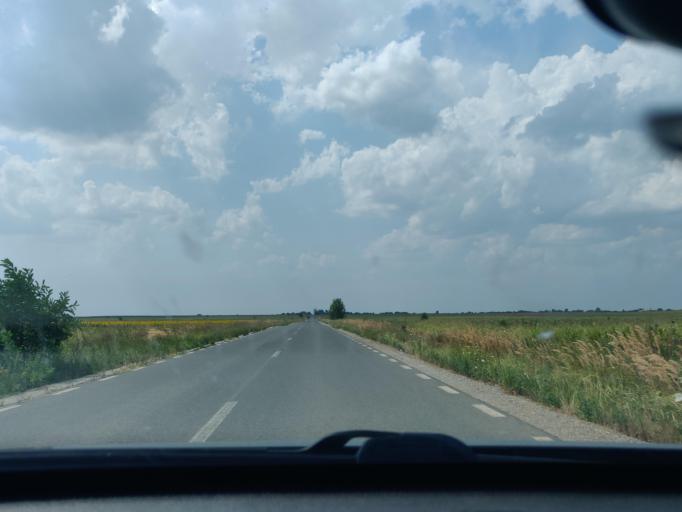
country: RO
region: Teleorman
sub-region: Comuna Gratia
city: Draghinesti
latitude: 44.4498
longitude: 25.4214
